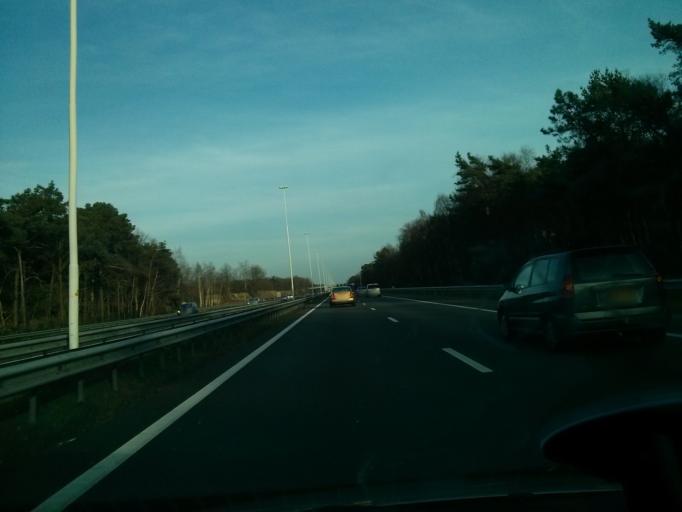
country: NL
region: North Brabant
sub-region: Gemeente Oirschot
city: Oirschot
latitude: 51.4928
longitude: 5.3275
